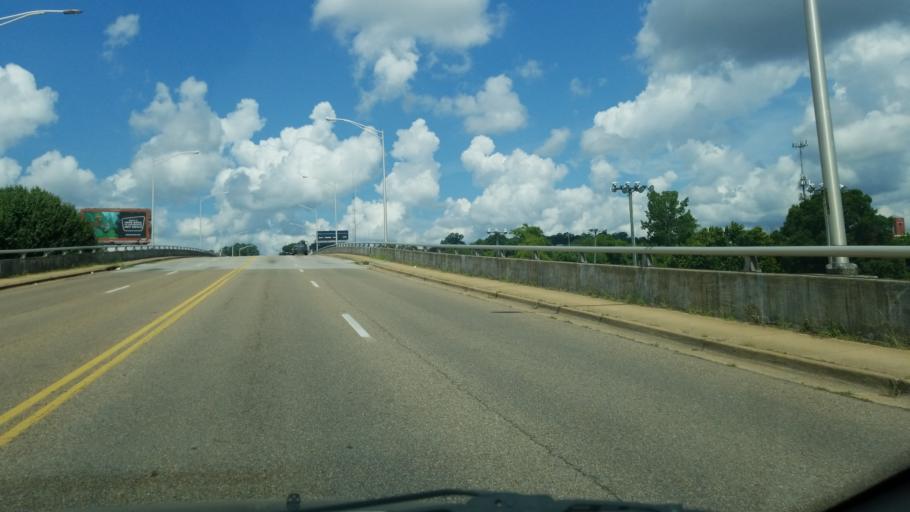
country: US
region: Tennessee
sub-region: Hamilton County
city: Chattanooga
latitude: 35.0400
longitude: -85.2857
